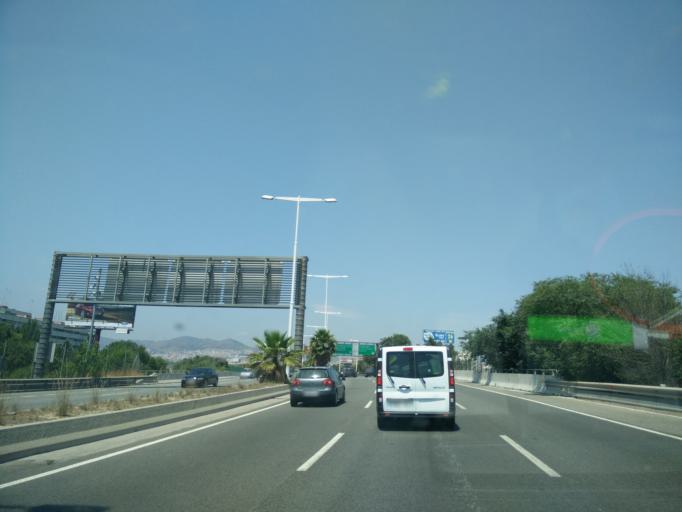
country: ES
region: Catalonia
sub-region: Provincia de Barcelona
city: Sant Adria de Besos
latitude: 41.4194
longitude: 2.2247
